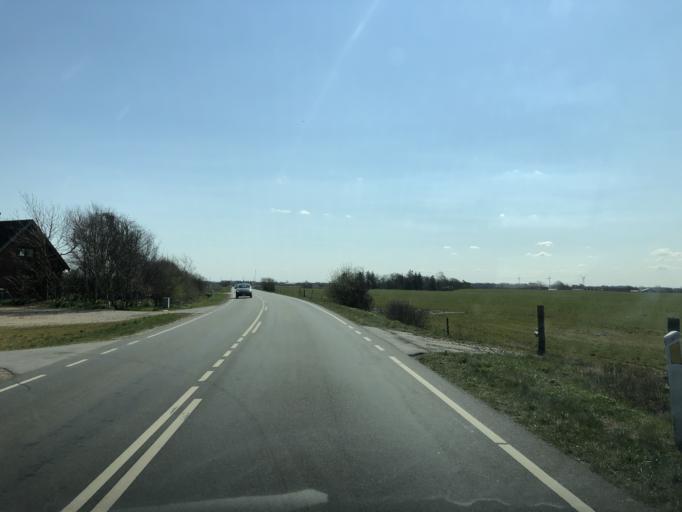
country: DK
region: Central Jutland
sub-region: Lemvig Kommune
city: Lemvig
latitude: 56.4345
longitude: 8.2977
